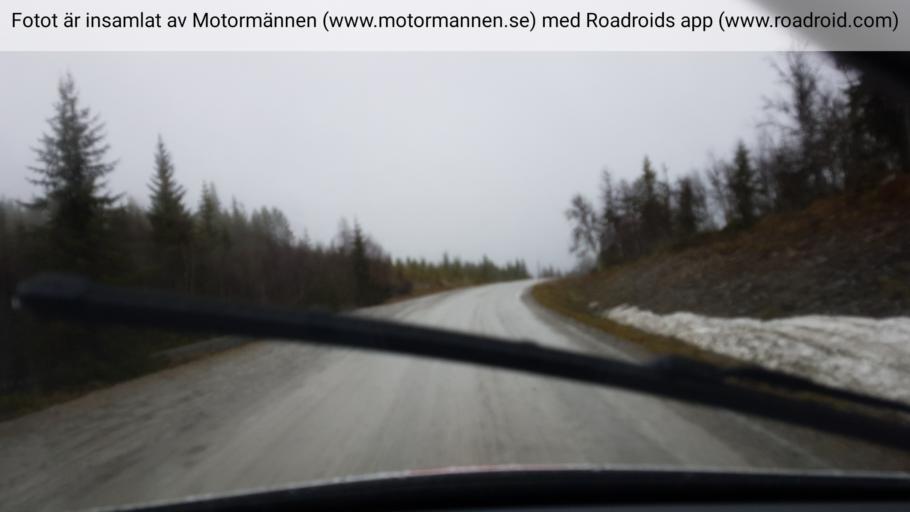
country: SE
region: Jaemtland
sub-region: Are Kommun
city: Are
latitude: 62.6285
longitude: 13.1190
